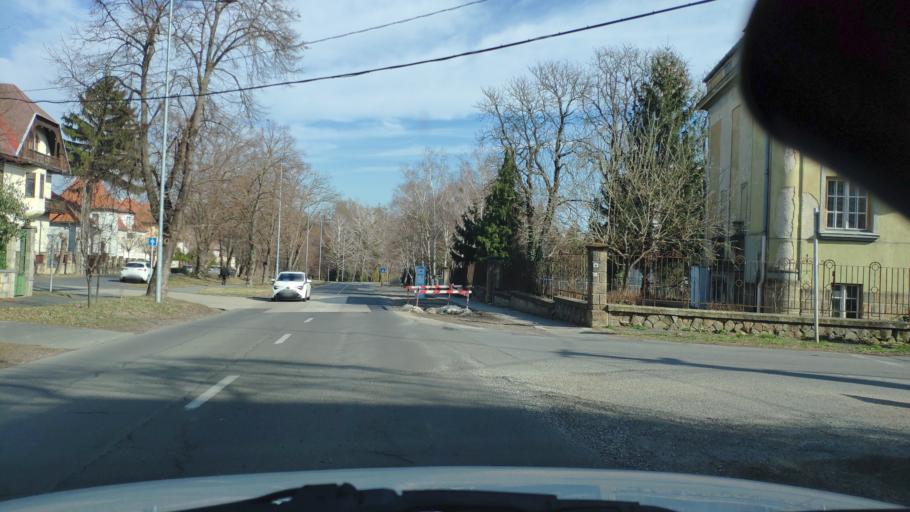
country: HU
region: Zala
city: Keszthely
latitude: 46.7591
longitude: 17.2427
